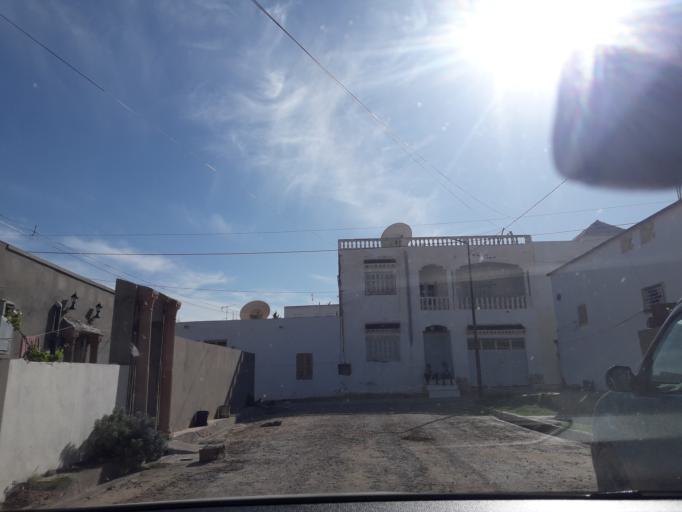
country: TN
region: Safaqis
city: Sfax
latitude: 34.7390
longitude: 10.5271
